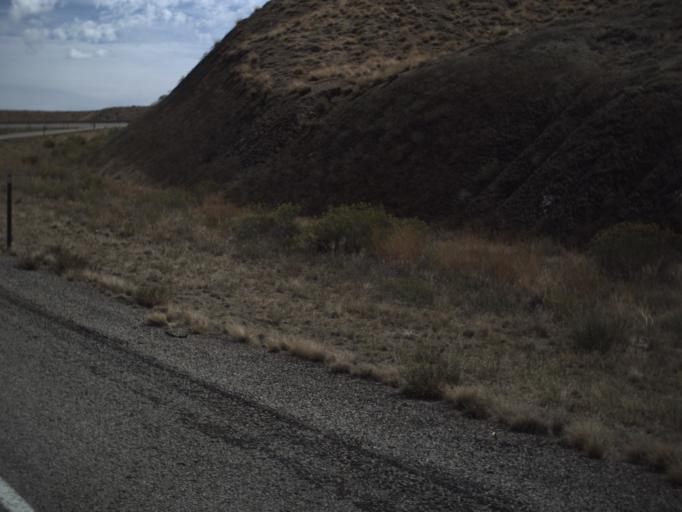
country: US
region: Utah
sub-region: Grand County
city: Moab
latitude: 38.9375
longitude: -109.8342
